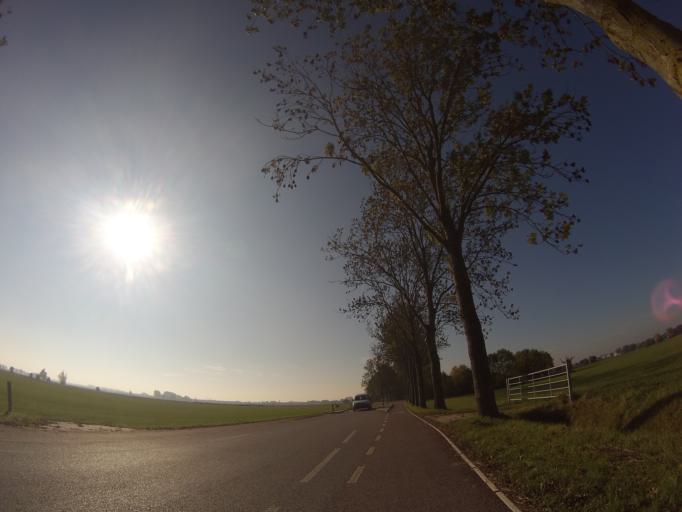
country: NL
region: Utrecht
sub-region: Gemeente Bunnik
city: Bunnik
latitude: 52.0381
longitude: 5.1979
